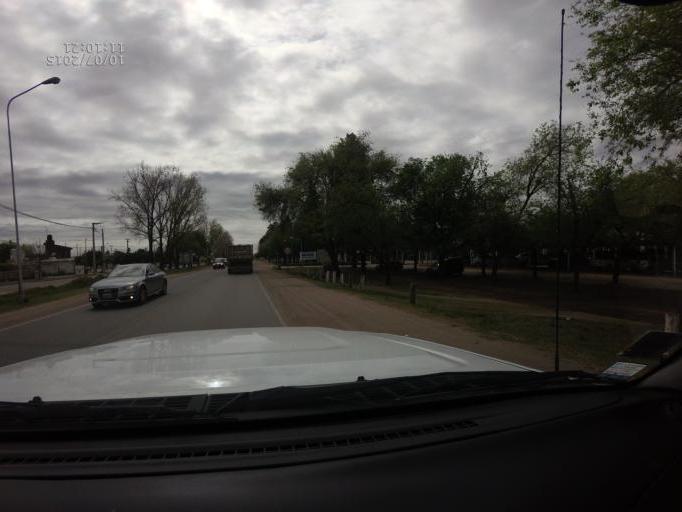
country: AR
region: Cordoba
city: Jesus Maria
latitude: -30.9900
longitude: -64.0958
